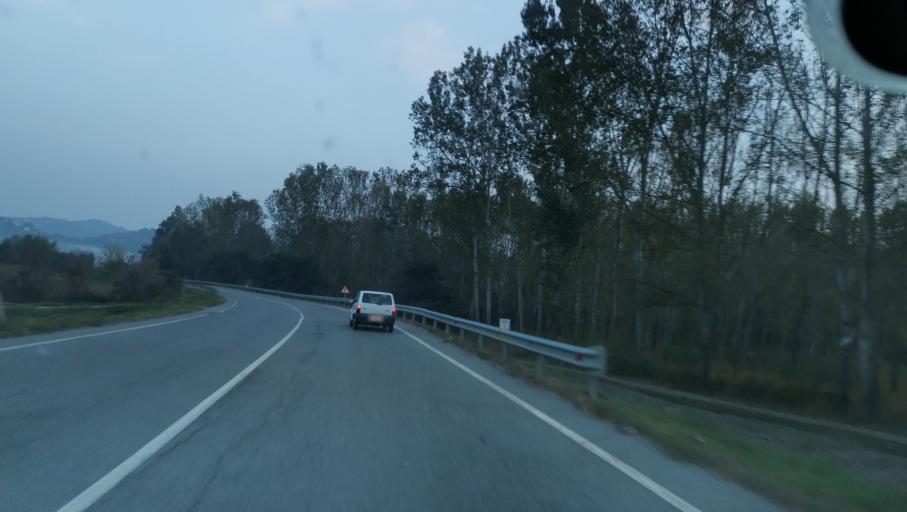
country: IT
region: Piedmont
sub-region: Provincia di Torino
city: Castiglione Torinese
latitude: 45.1270
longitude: 7.7860
